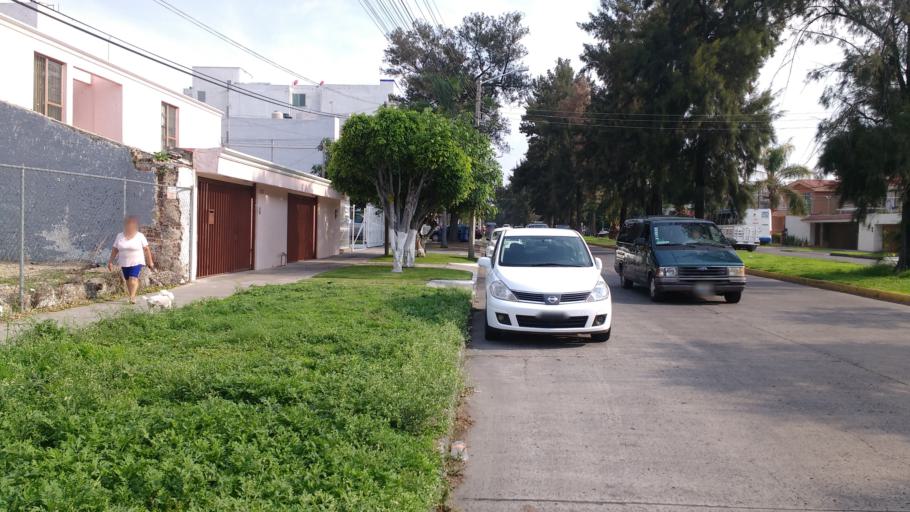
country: MX
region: Jalisco
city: Guadalajara
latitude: 20.6477
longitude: -103.3937
